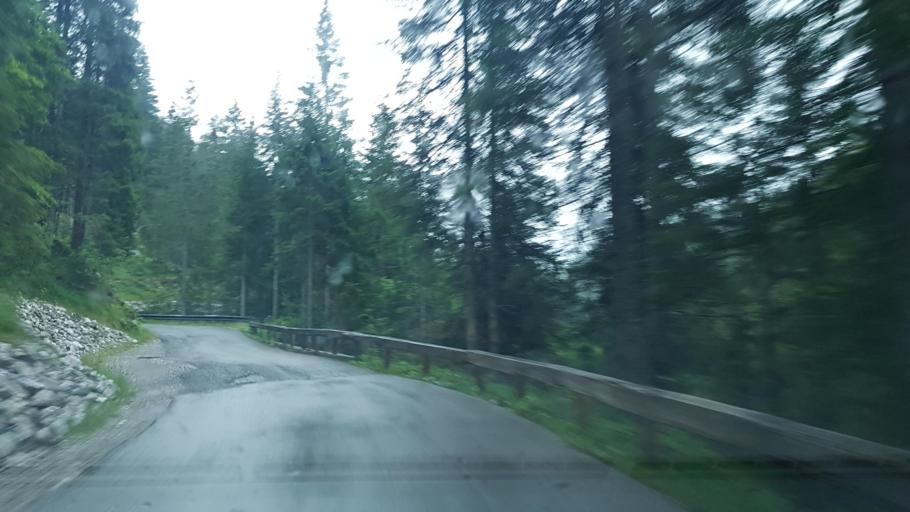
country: IT
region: Veneto
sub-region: Provincia di Belluno
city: Granvilla
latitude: 46.5814
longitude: 12.7265
